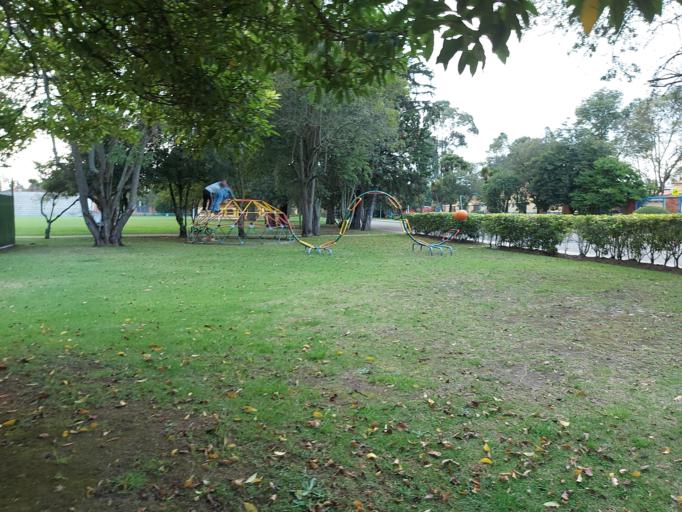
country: CO
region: Cundinamarca
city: Cota
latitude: 4.7927
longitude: -74.0460
